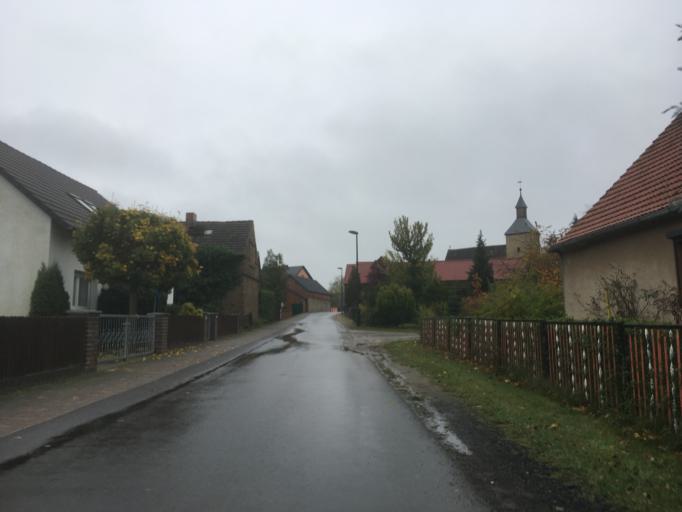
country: DE
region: Brandenburg
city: Neu Zauche
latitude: 52.0302
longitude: 14.0761
